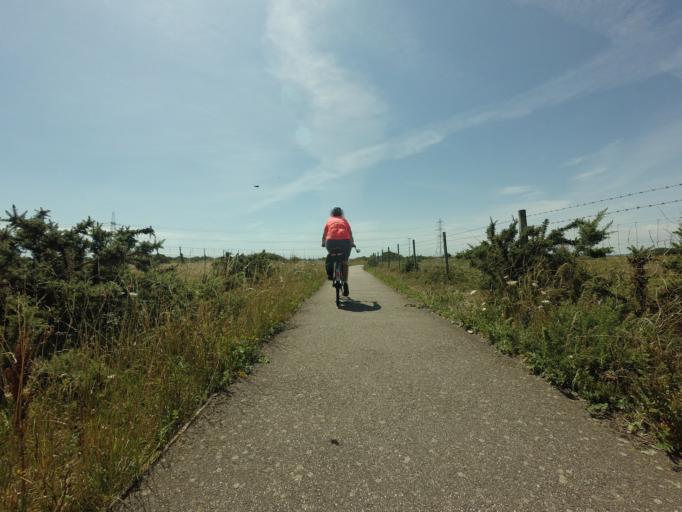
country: GB
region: England
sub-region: Kent
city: Lydd
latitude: 50.9454
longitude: 0.8887
